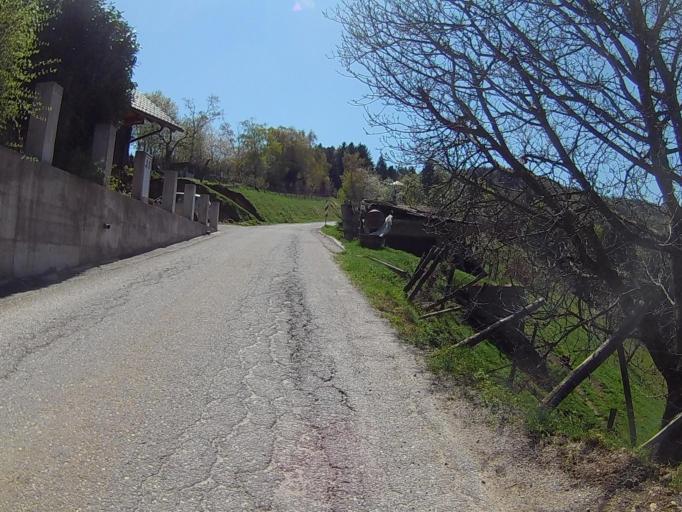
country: SI
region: Ruse
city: Ruse
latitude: 46.5233
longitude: 15.5258
